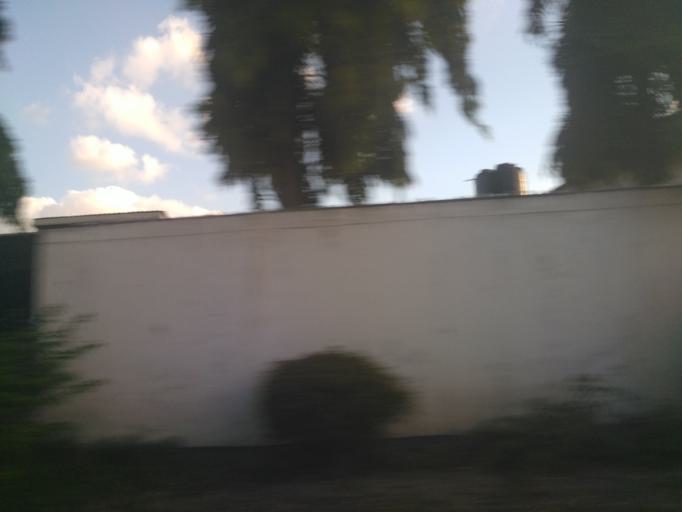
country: TZ
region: Dar es Salaam
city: Dar es Salaam
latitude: -6.8590
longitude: 39.2619
